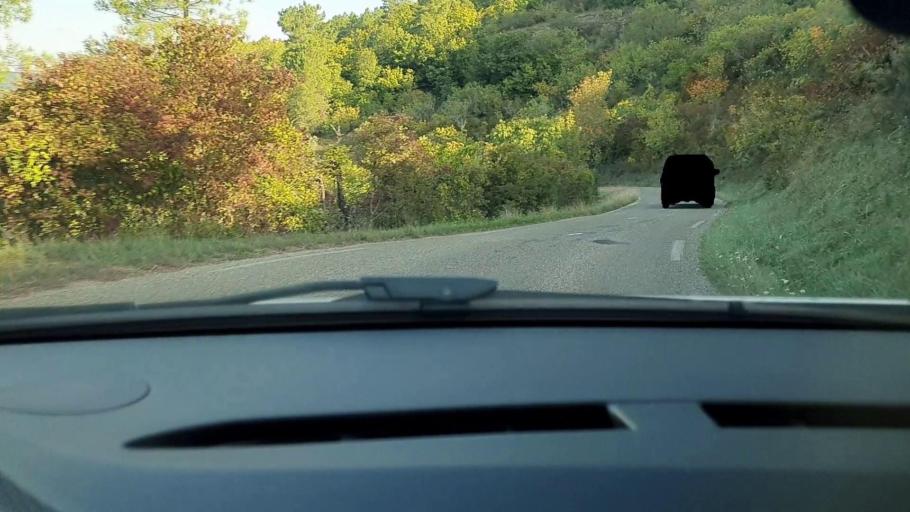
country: FR
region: Languedoc-Roussillon
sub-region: Departement du Gard
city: Besseges
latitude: 44.3116
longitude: 4.1407
